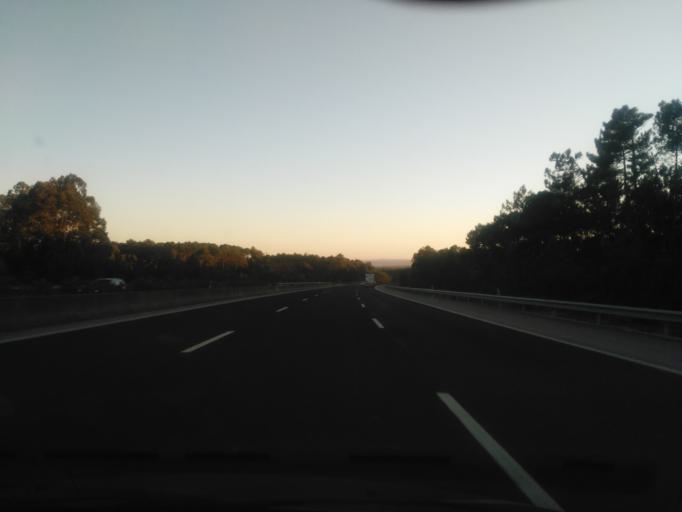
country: PT
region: Leiria
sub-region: Leiria
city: Maceira
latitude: 39.6839
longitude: -8.9356
